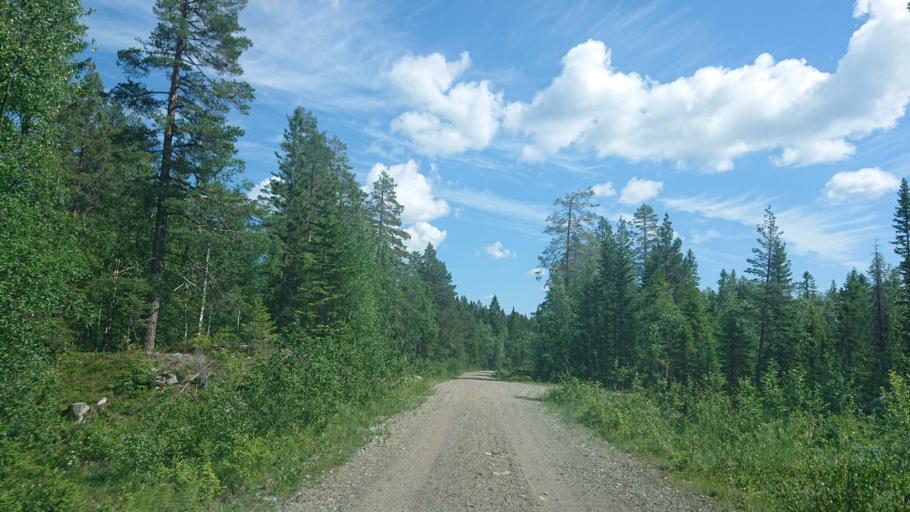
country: SE
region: Vaesternorrland
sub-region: Solleftea Kommun
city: Solleftea
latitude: 62.9341
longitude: 17.0795
